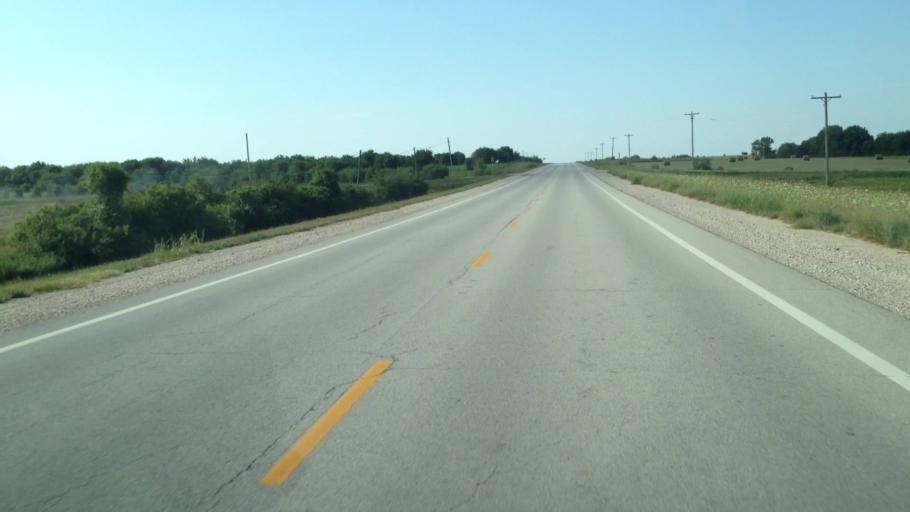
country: US
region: Kansas
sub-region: Anderson County
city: Garnett
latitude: 38.1093
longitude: -95.2428
